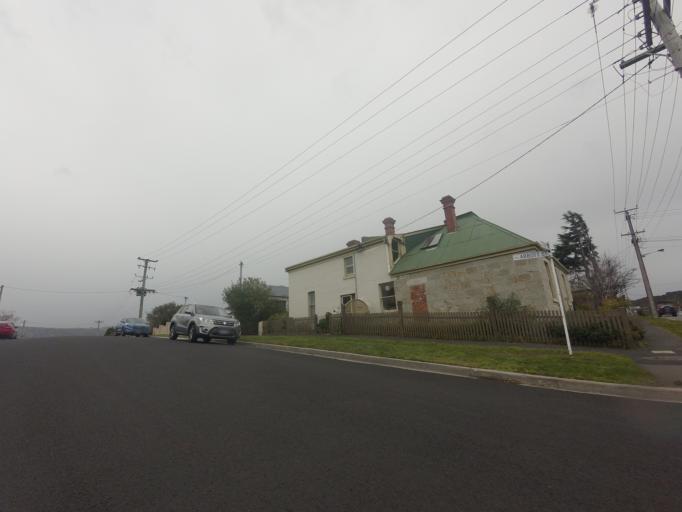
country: AU
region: Tasmania
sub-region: Clarence
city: Bellerive
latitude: -42.8787
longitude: 147.3678
